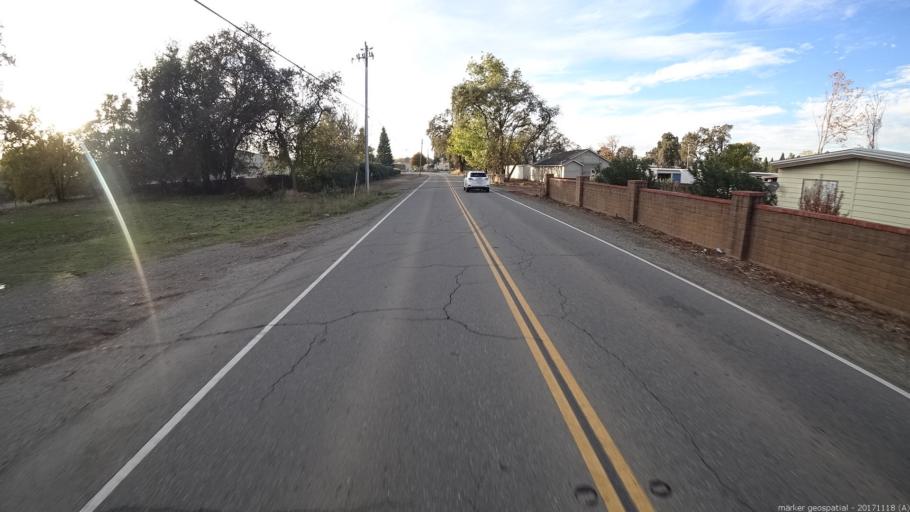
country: US
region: California
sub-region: Shasta County
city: Anderson
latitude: 40.4684
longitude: -122.3142
